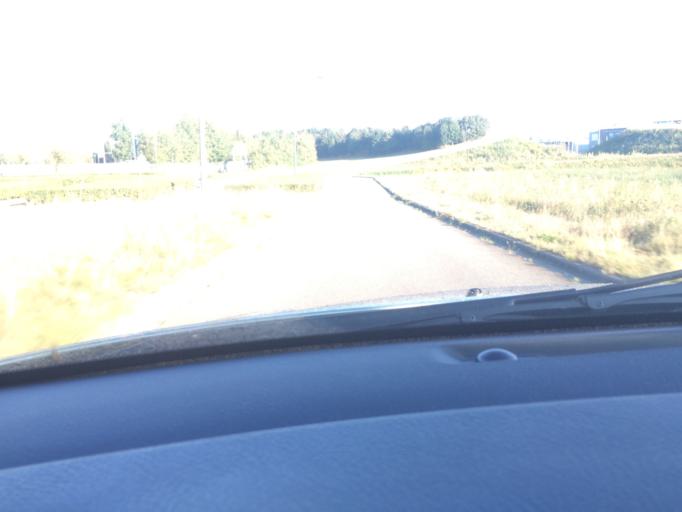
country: NL
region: North Brabant
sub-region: Gemeente Waalwijk
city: Waalwijk
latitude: 51.6760
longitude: 5.0483
